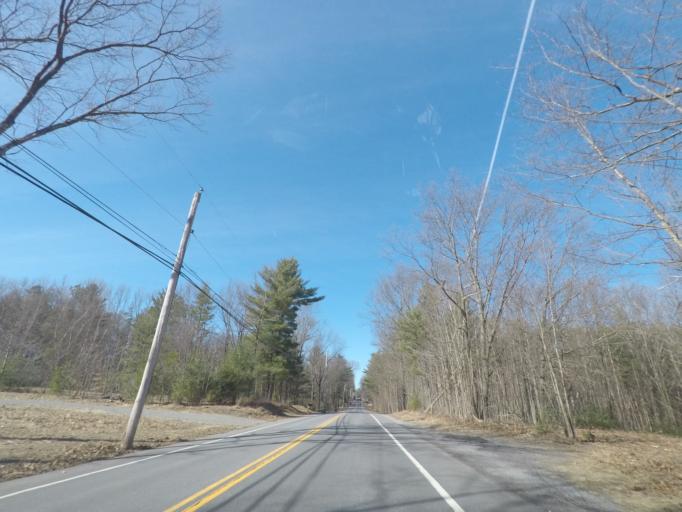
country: US
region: New York
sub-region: Saratoga County
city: North Ballston Spa
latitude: 43.0187
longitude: -73.8488
